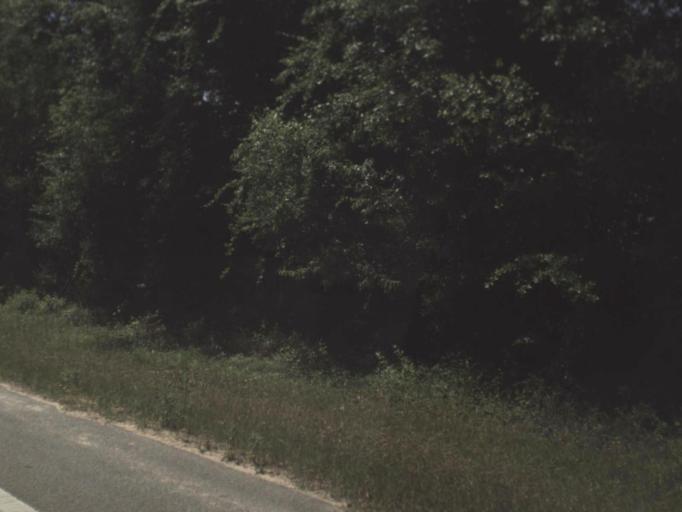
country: US
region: Florida
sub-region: Jackson County
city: Marianna
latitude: 30.6708
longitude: -85.2378
